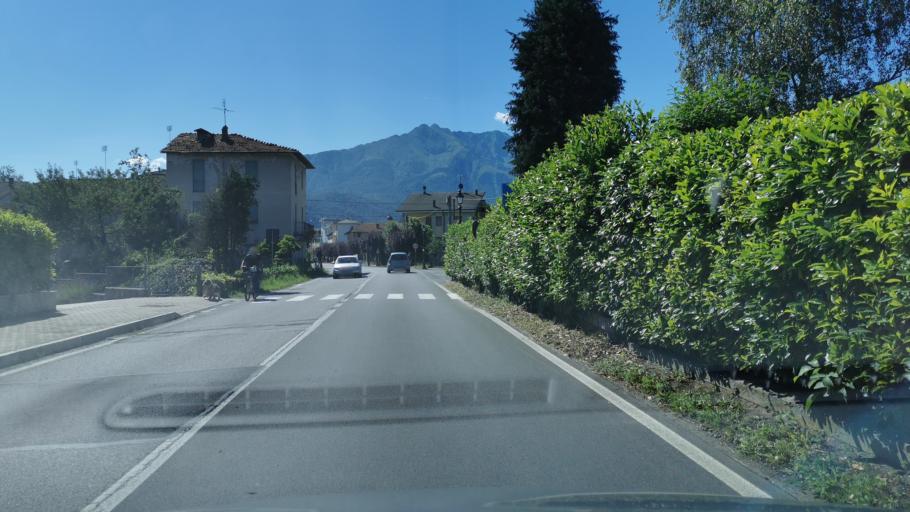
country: IT
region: Piedmont
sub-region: Provincia di Cuneo
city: Boves
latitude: 44.3329
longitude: 7.5466
